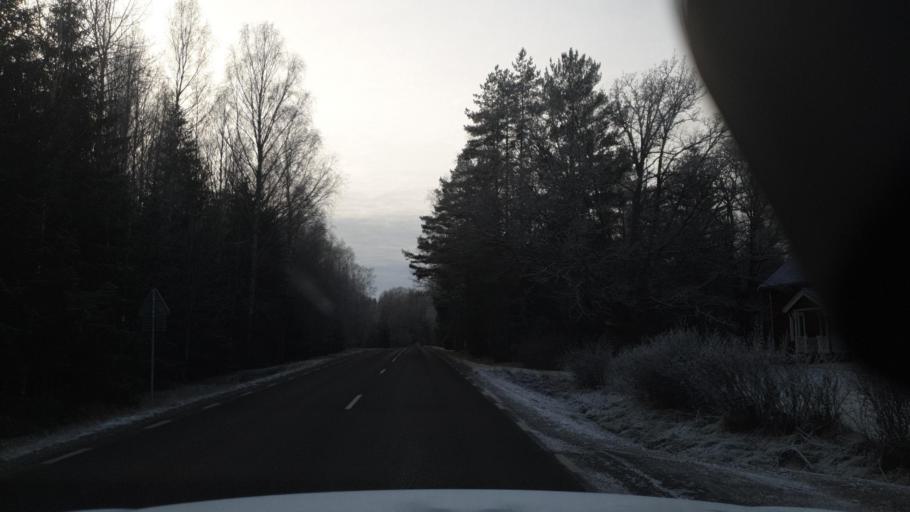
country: SE
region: Vaermland
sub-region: Eda Kommun
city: Amotfors
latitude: 59.7040
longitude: 12.4339
